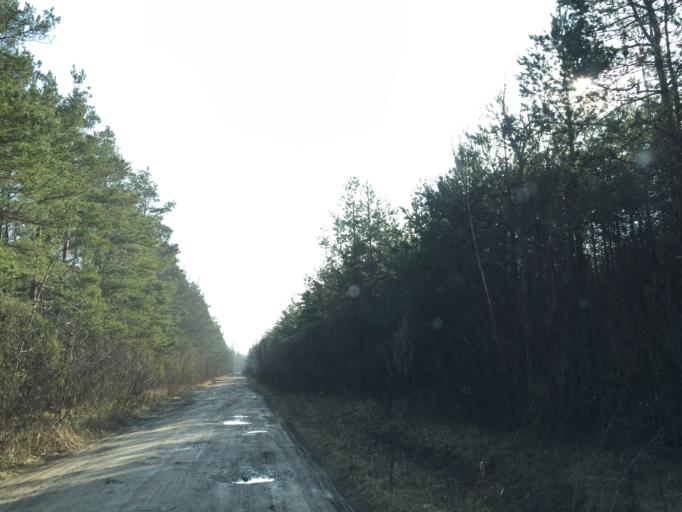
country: EE
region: Saare
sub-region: Kuressaare linn
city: Kuressaare
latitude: 58.2381
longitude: 22.4474
